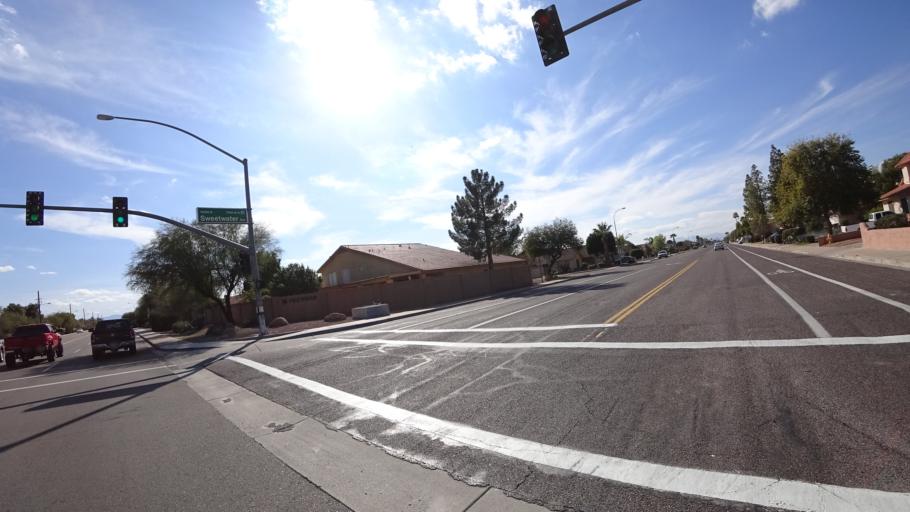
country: US
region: Arizona
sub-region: Maricopa County
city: Peoria
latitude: 33.6032
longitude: -112.2202
